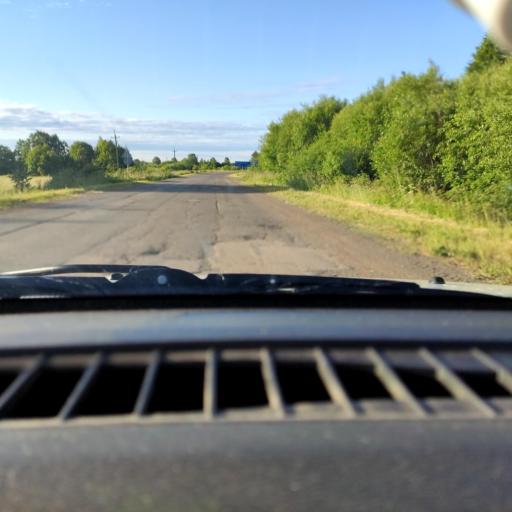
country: RU
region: Perm
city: Uinskoye
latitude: 57.0892
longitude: 56.5569
